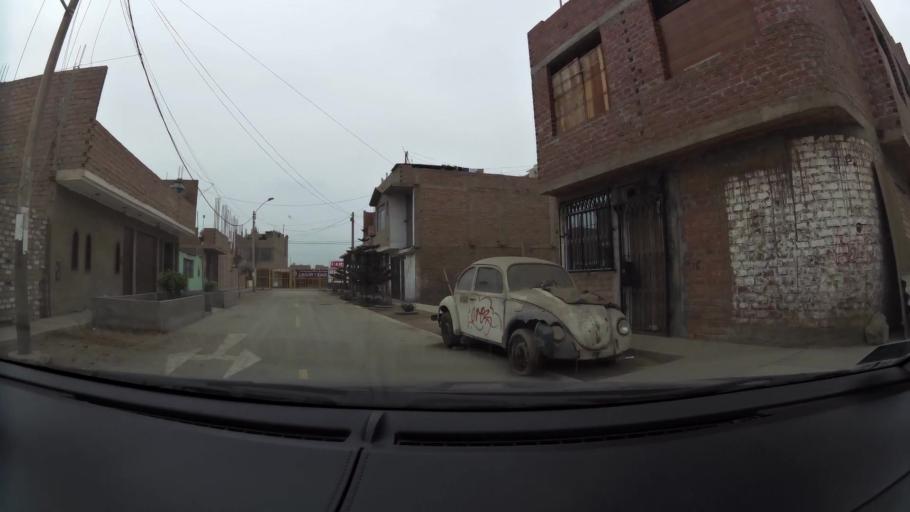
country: PE
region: Lima
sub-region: Lima
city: Independencia
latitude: -11.9513
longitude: -77.0898
